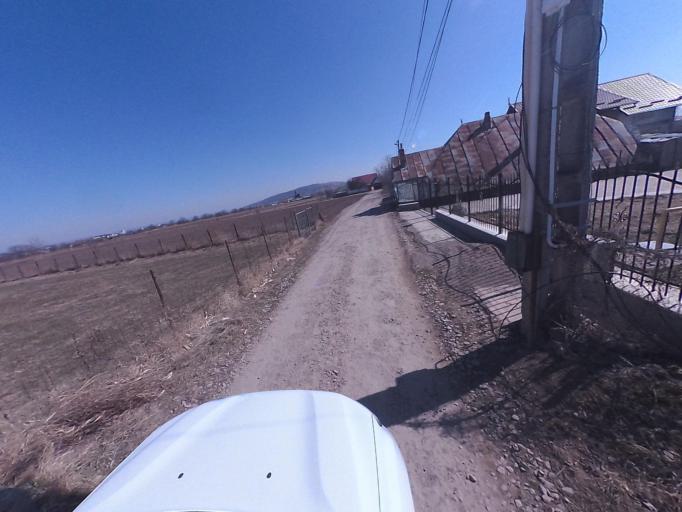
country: RO
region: Neamt
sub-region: Oras Targu Neamt
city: Humulesti
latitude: 47.1930
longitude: 26.3523
